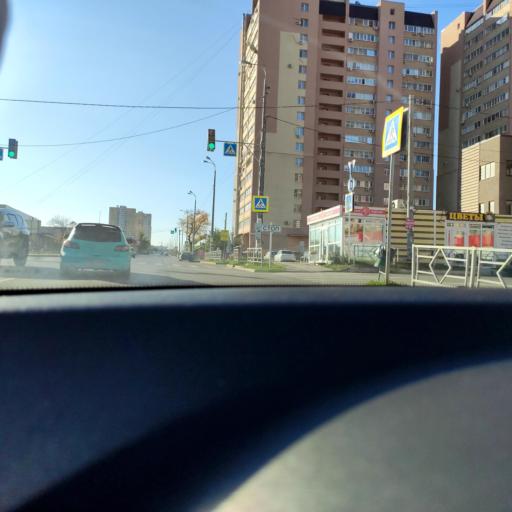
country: RU
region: Samara
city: Samara
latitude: 53.2062
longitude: 50.2053
